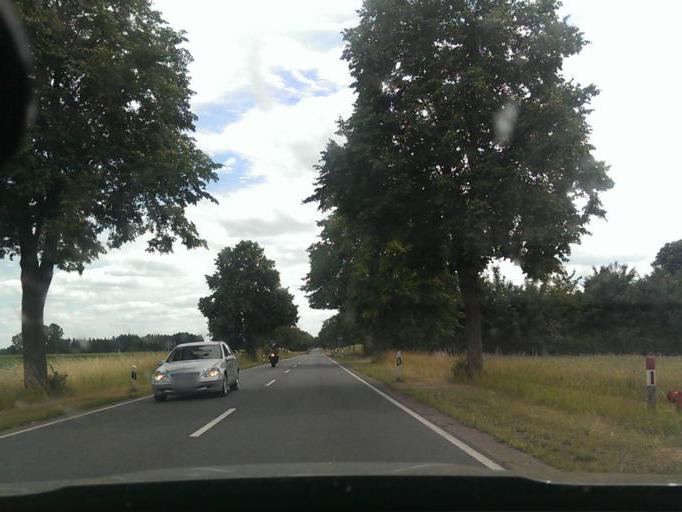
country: DE
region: Lower Saxony
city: Oyten
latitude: 53.0400
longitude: 9.0338
